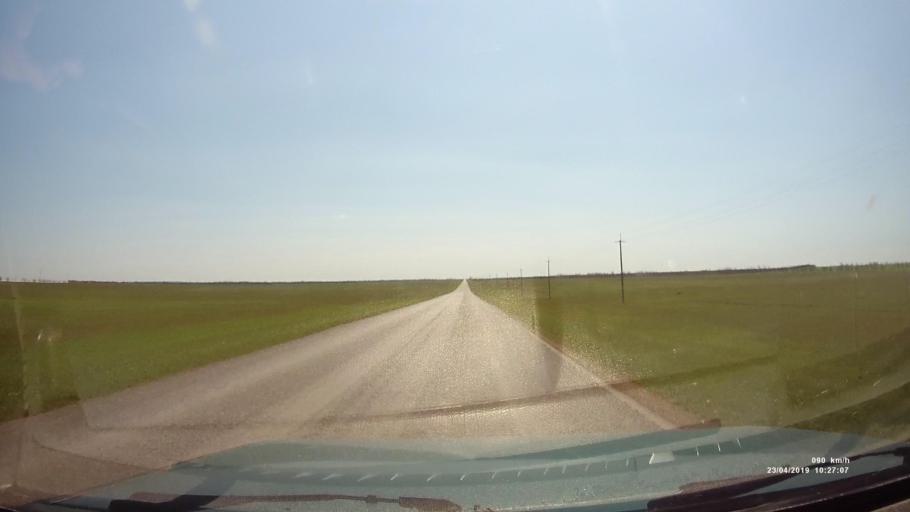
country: RU
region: Kalmykiya
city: Yashalta
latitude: 46.6163
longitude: 42.4860
